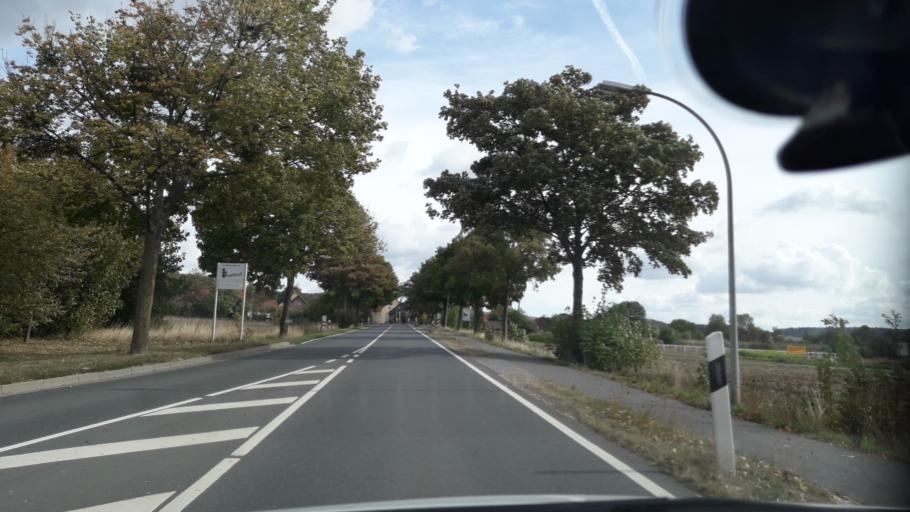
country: DE
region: Lower Saxony
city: Liebenburg
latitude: 52.0068
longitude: 10.3812
